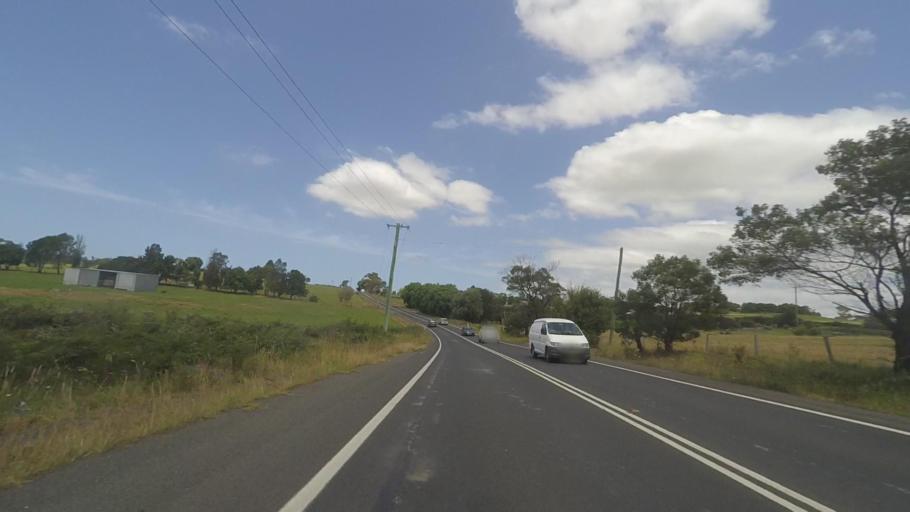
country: AU
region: New South Wales
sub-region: Shoalhaven Shire
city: Milton
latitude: -35.2896
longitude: 150.4208
